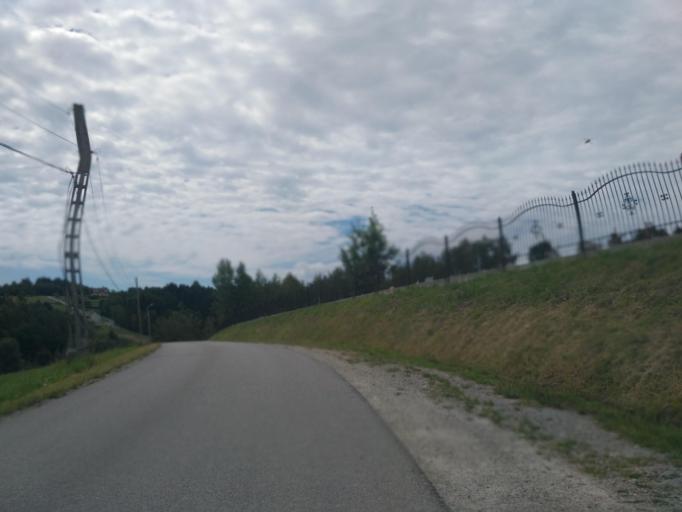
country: PL
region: Subcarpathian Voivodeship
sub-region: Powiat rzeszowski
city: Straszydle
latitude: 49.8958
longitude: 21.9807
